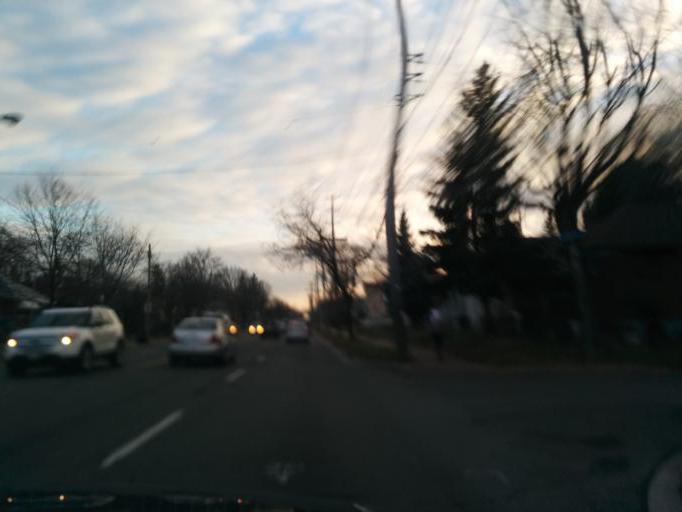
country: CA
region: Ontario
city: Etobicoke
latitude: 43.6431
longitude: -79.5228
